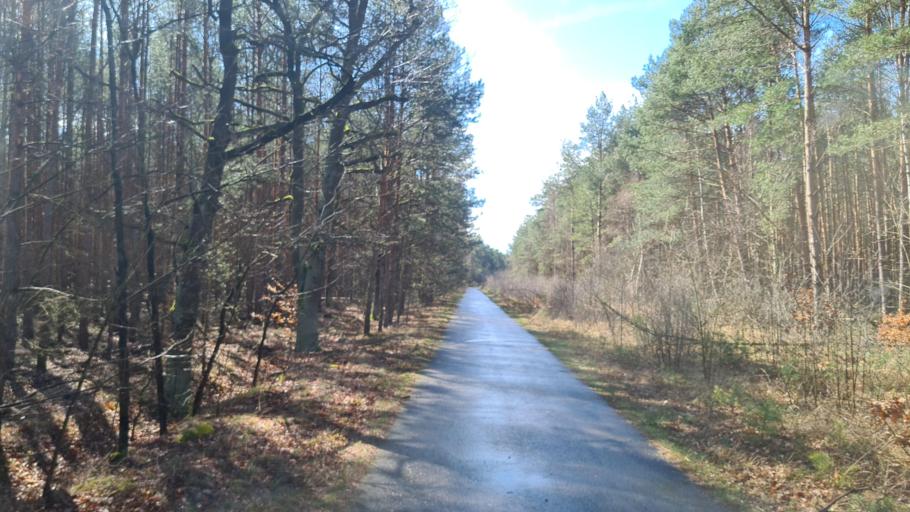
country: DE
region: Brandenburg
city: Altdobern
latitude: 51.7023
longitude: 14.0377
